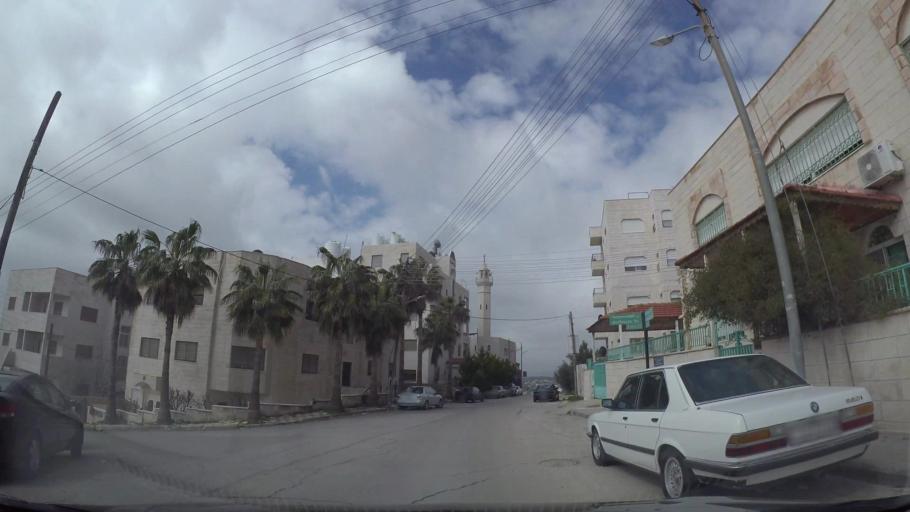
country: JO
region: Amman
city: Wadi as Sir
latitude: 31.9492
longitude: 35.8268
